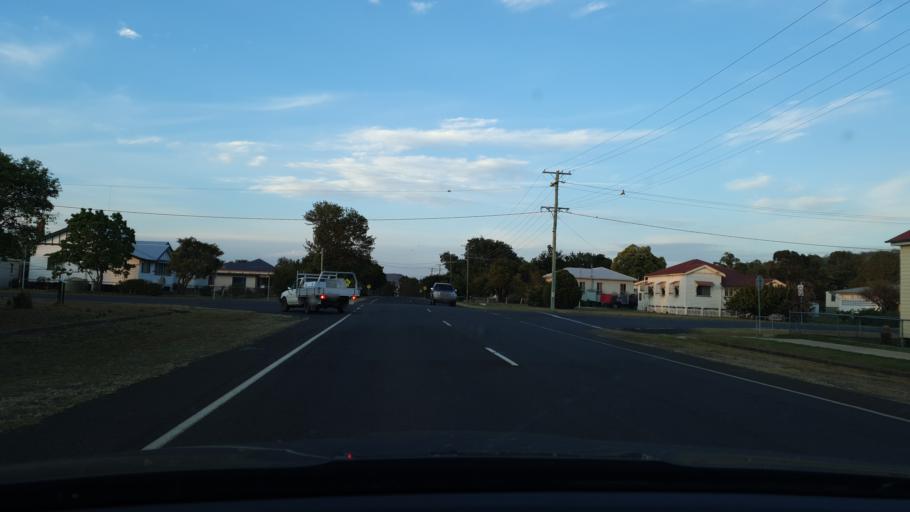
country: AU
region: Queensland
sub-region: Southern Downs
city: Warwick
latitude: -28.0336
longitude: 151.9807
